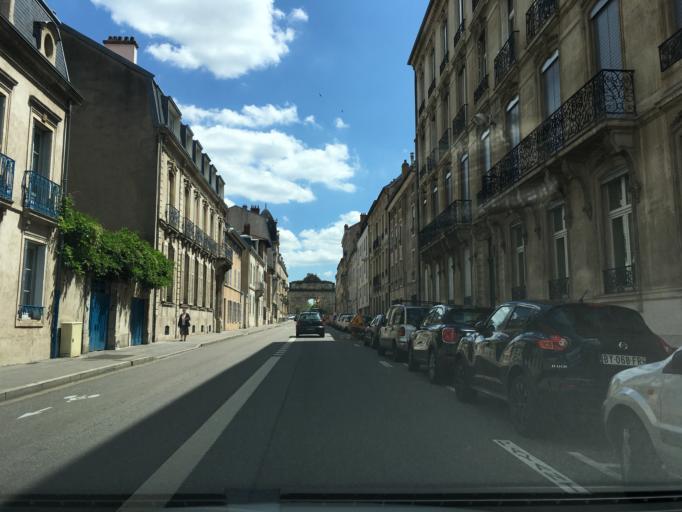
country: FR
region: Lorraine
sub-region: Departement de Meurthe-et-Moselle
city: Maxeville
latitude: 48.6998
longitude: 6.1729
